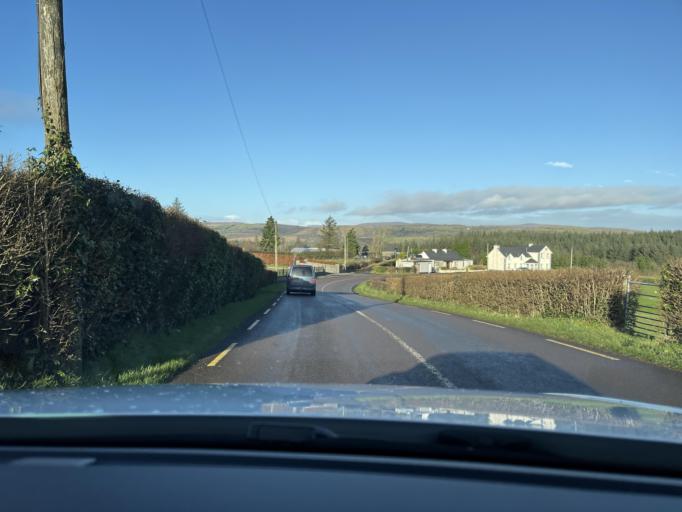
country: IE
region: Connaught
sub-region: County Leitrim
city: Manorhamilton
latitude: 54.3011
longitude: -8.2454
